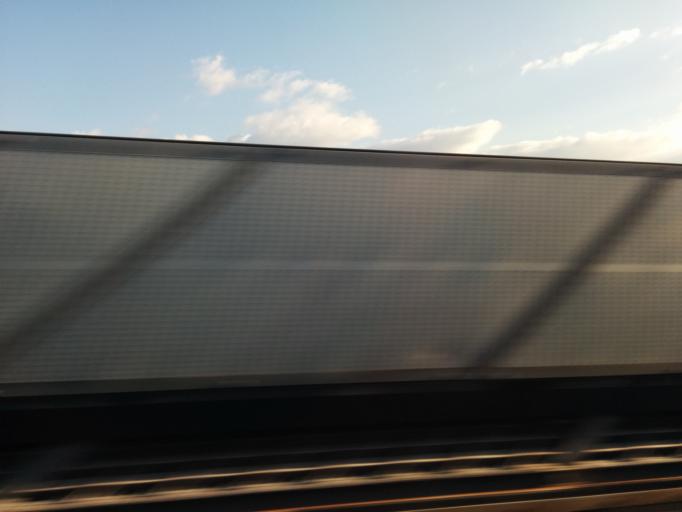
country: JP
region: Aichi
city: Obu
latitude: 35.0248
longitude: 136.9853
